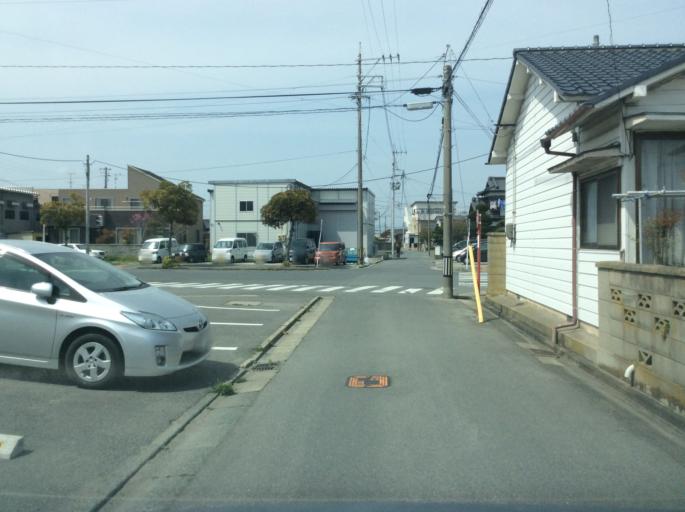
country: JP
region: Fukushima
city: Iwaki
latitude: 36.9486
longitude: 140.8916
